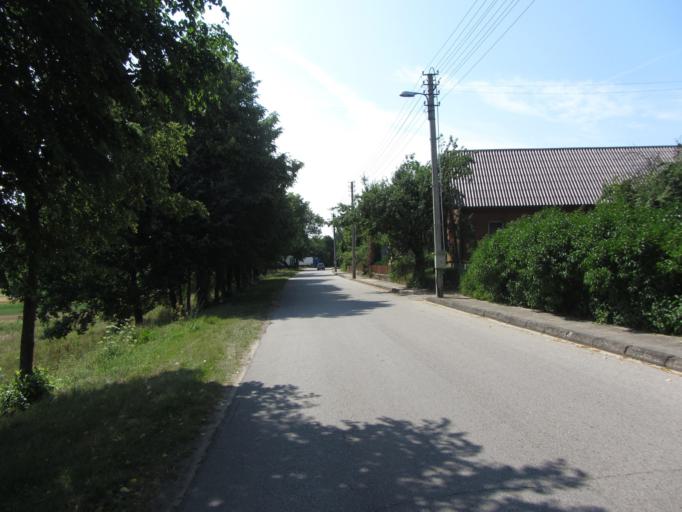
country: LT
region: Alytaus apskritis
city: Druskininkai
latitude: 53.9787
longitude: 23.9425
